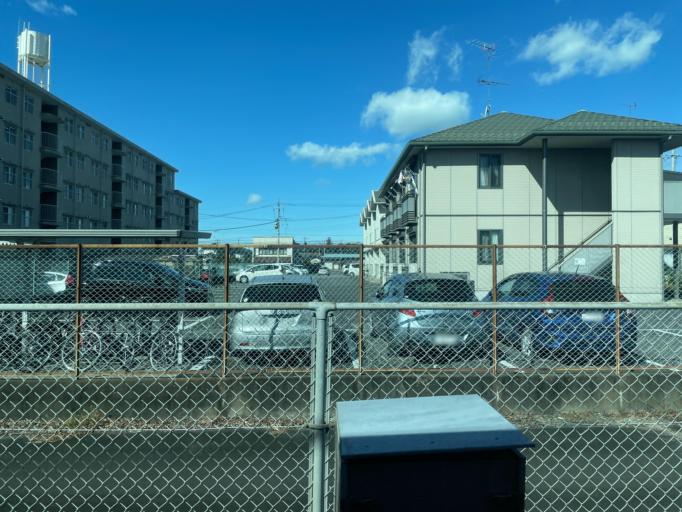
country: JP
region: Tochigi
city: Oyama
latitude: 36.2592
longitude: 139.7620
